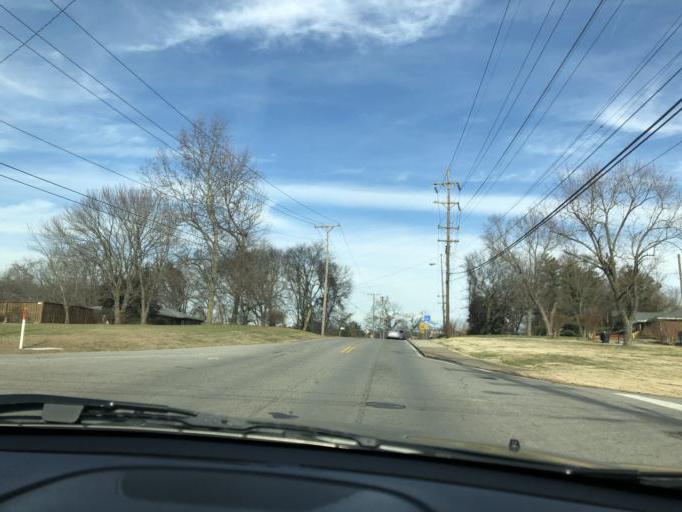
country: US
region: Tennessee
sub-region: Davidson County
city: Lakewood
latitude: 36.1816
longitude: -86.6778
